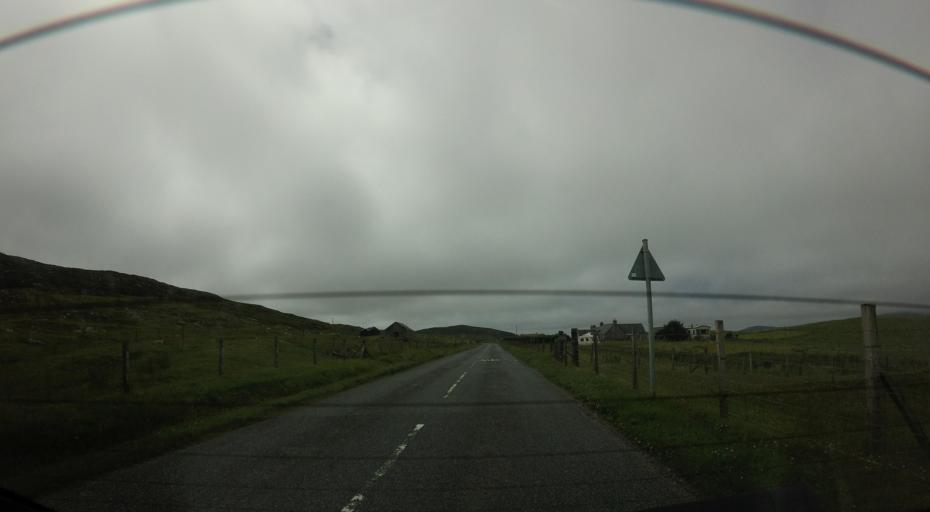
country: GB
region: Scotland
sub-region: Eilean Siar
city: Harris
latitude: 57.8690
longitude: -6.9350
